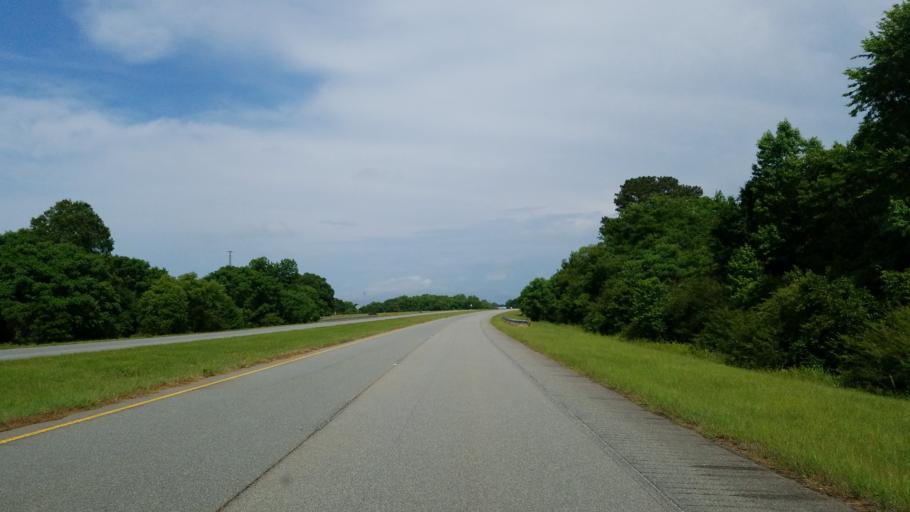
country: US
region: Georgia
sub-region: Houston County
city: Perry
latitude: 32.4356
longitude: -83.7700
